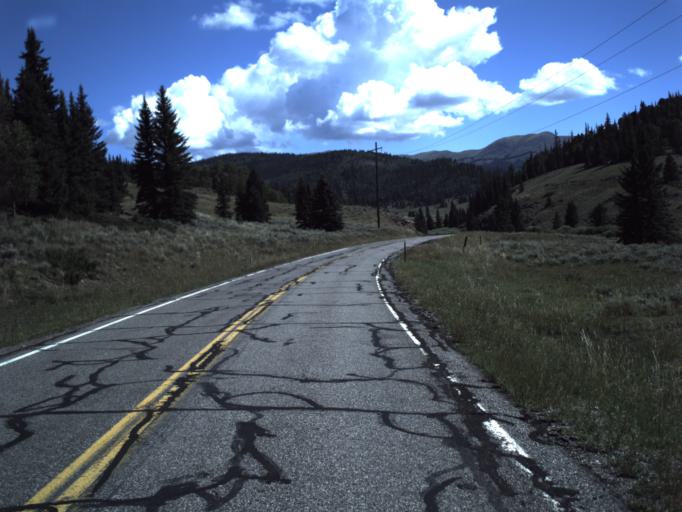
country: US
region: Utah
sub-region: Beaver County
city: Beaver
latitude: 38.2925
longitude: -112.4421
